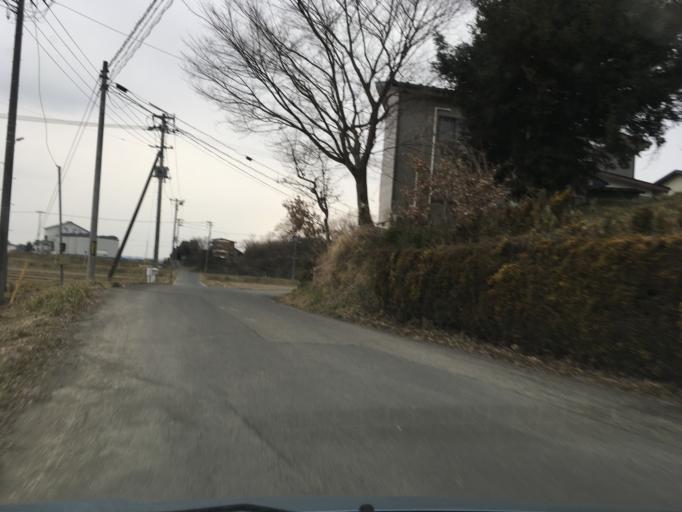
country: JP
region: Miyagi
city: Wakuya
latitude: 38.6658
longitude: 141.2757
